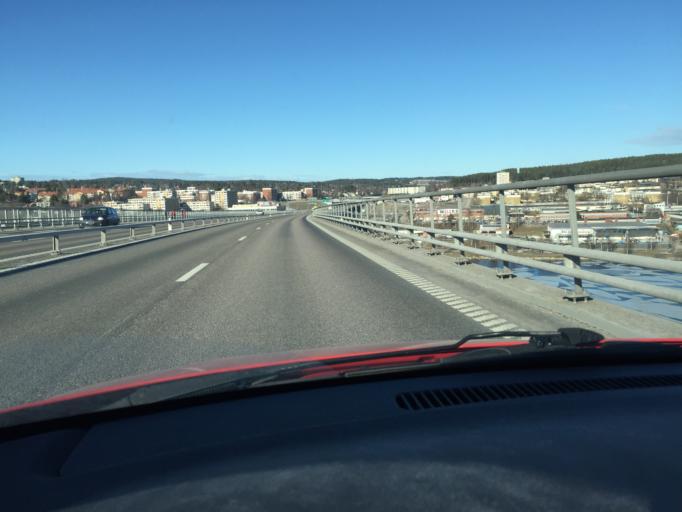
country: SE
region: Vaesternorrland
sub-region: Sundsvalls Kommun
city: Sundsvall
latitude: 62.3912
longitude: 17.3394
